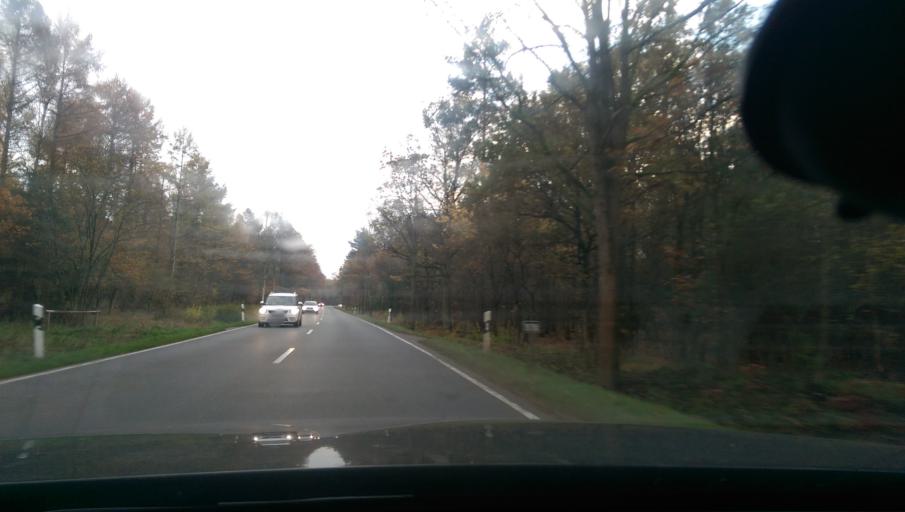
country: DE
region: Lower Saxony
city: Hambuhren
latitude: 52.6177
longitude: 9.9296
